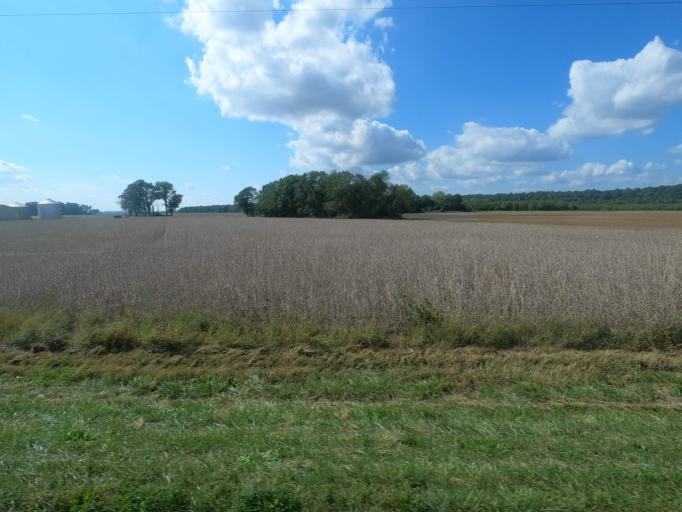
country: US
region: Illinois
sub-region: Massac County
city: Metropolis
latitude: 37.2934
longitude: -88.7556
